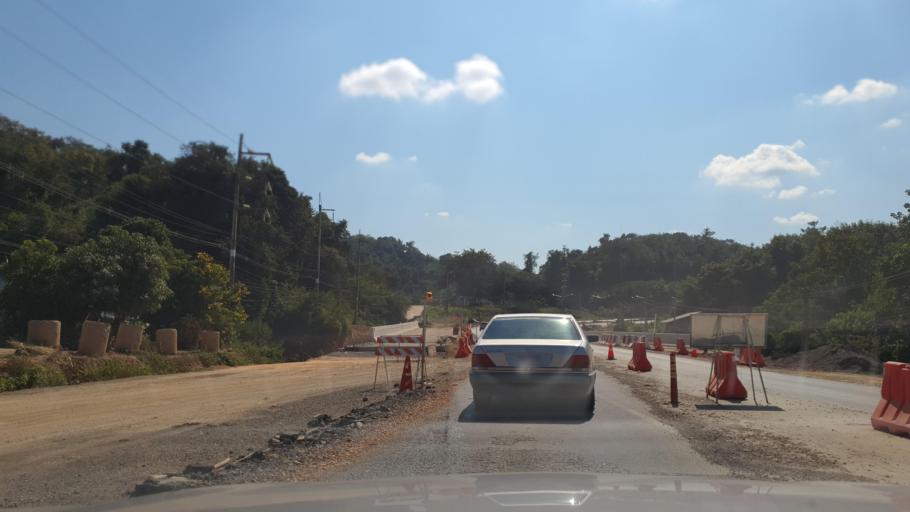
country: TH
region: Nan
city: Nan
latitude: 18.9207
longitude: 100.7656
